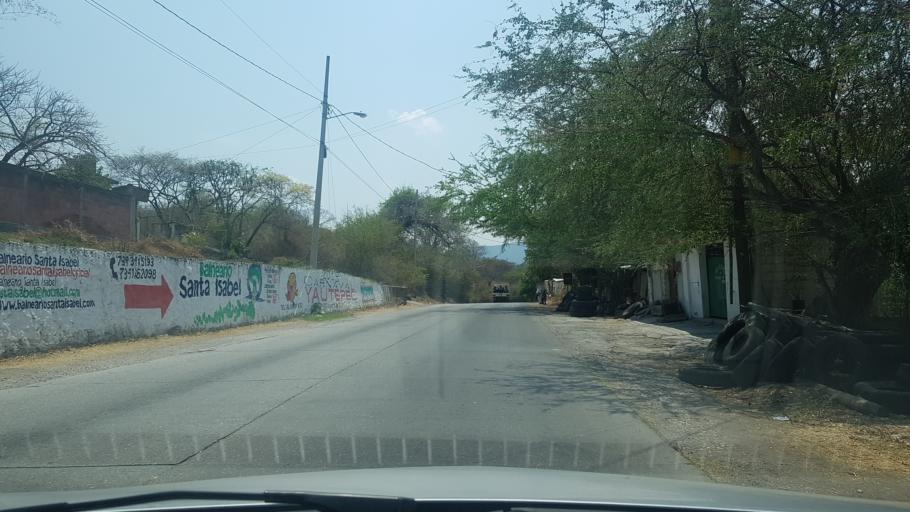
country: MX
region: Morelos
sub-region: Jiutepec
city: Independencia
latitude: 18.8046
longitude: -99.0912
